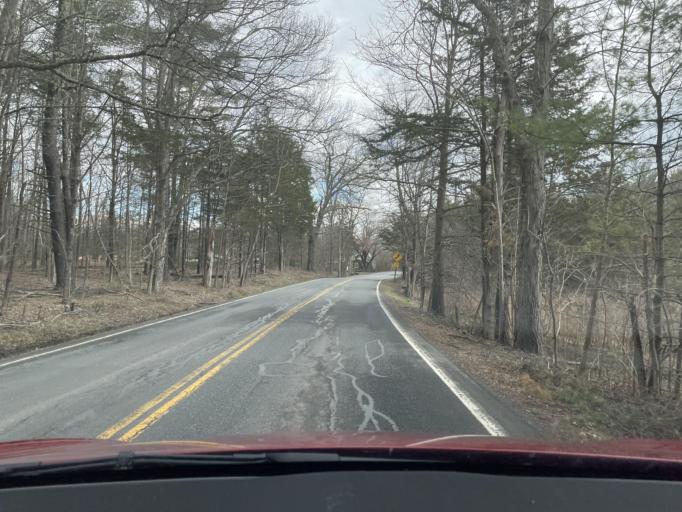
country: US
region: New York
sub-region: Ulster County
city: Zena
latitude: 42.0475
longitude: -74.0534
